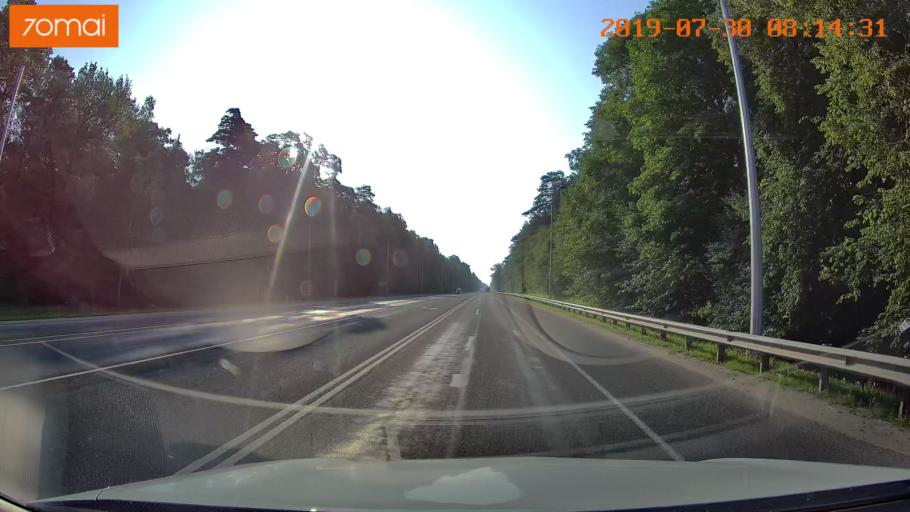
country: RU
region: Kaliningrad
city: Zheleznodorozhnyy
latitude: 54.6478
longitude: 21.3600
